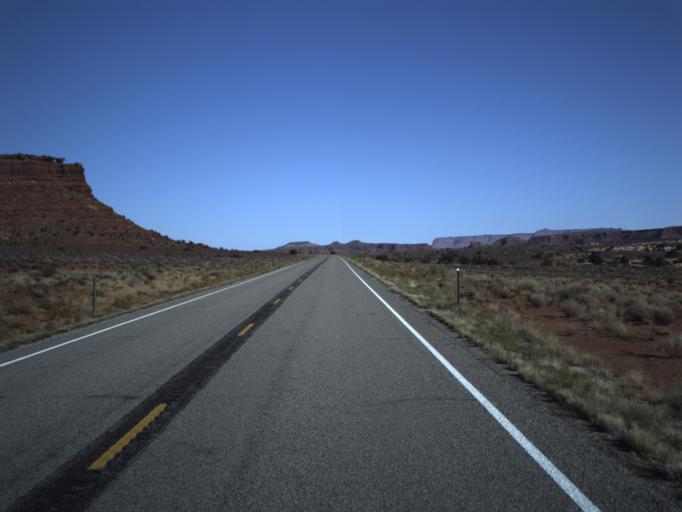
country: US
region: Utah
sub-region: San Juan County
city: Blanding
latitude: 37.7691
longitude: -110.2867
